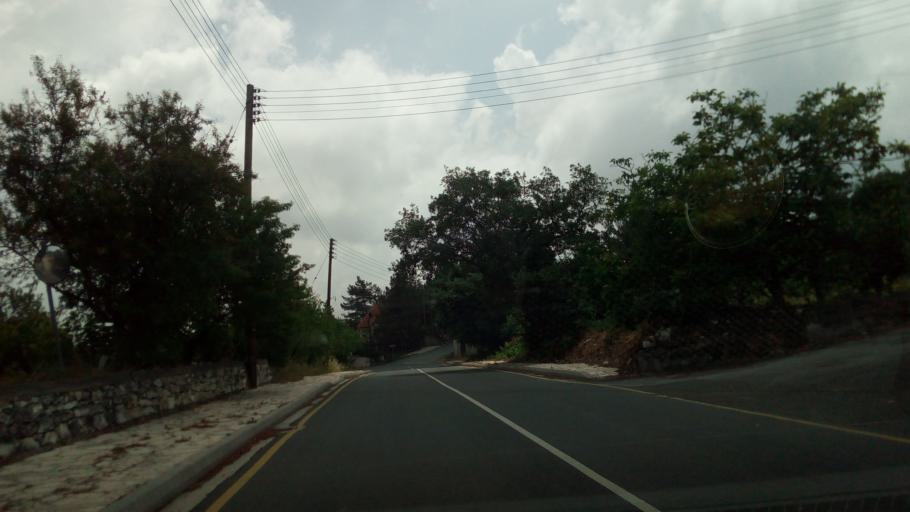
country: CY
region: Limassol
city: Pelendri
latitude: 34.8590
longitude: 32.8792
